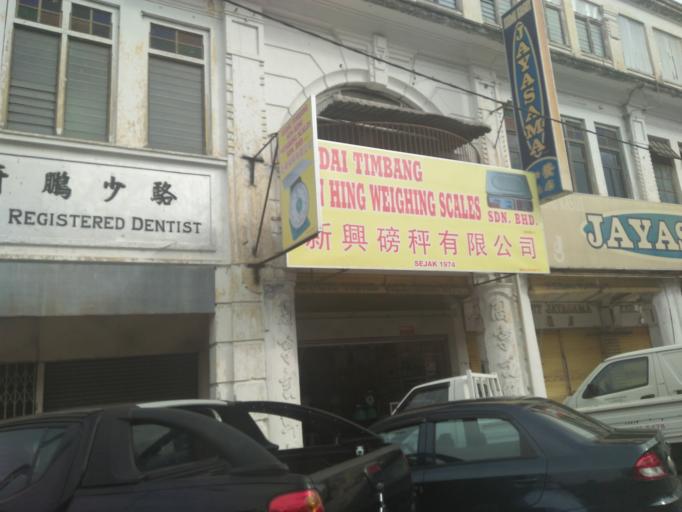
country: MY
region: Perak
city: Ipoh
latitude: 4.5955
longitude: 101.0812
